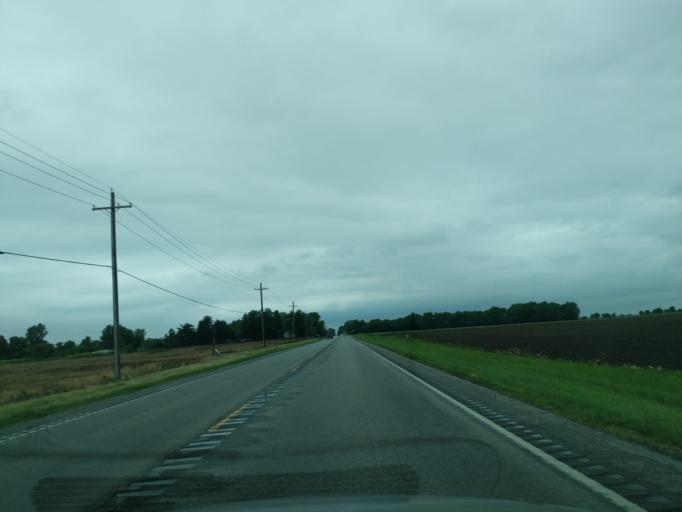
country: US
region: Indiana
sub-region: Hamilton County
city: Cicero
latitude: 40.1141
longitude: -86.0136
